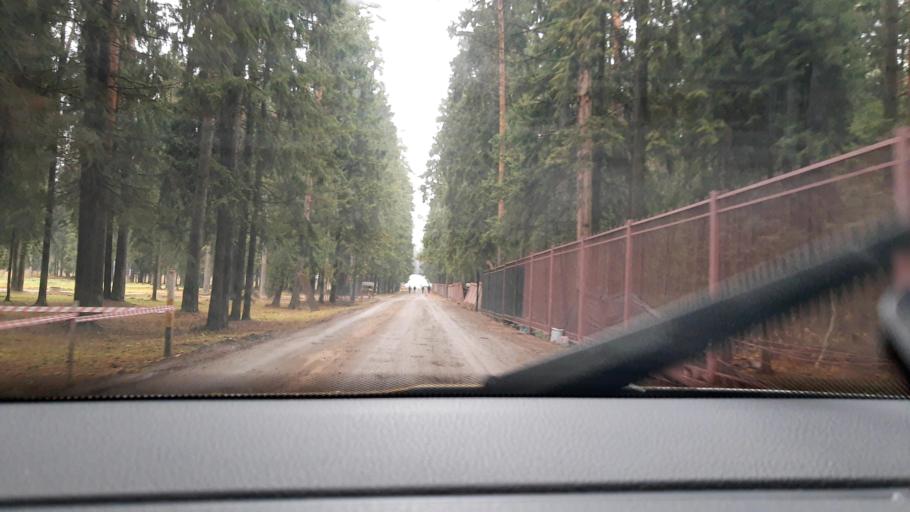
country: RU
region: Moskovskaya
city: Pushkino
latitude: 56.0088
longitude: 37.8894
